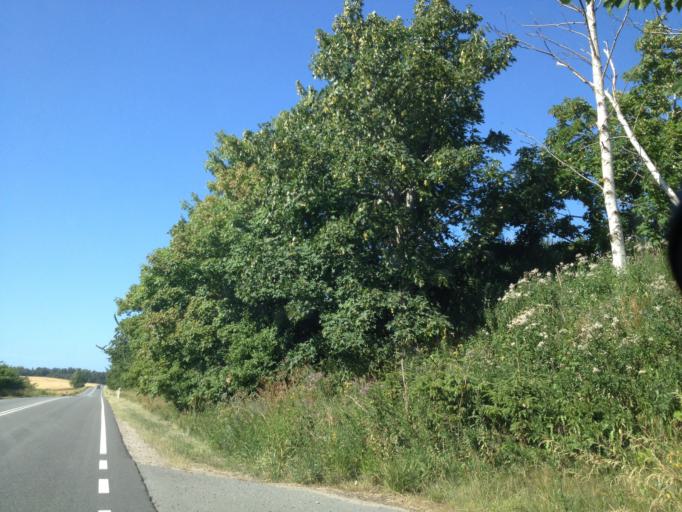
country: DK
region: Capital Region
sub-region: Gribskov Kommune
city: Gilleleje
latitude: 56.0727
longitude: 12.3452
